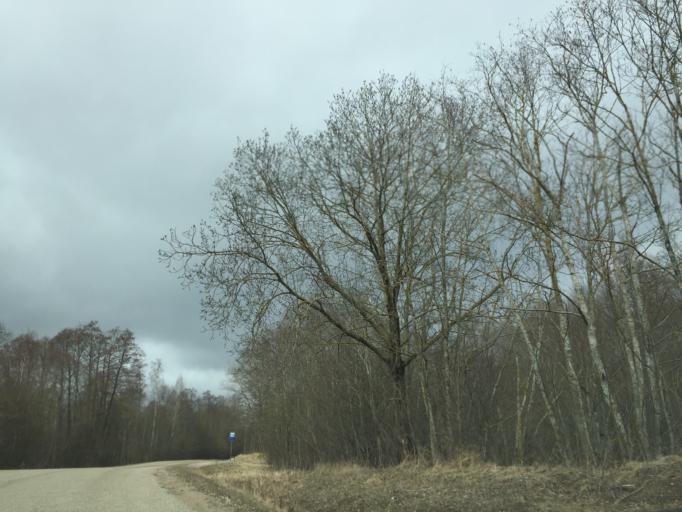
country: LV
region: Ilukste
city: Ilukste
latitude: 56.0192
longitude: 26.2378
